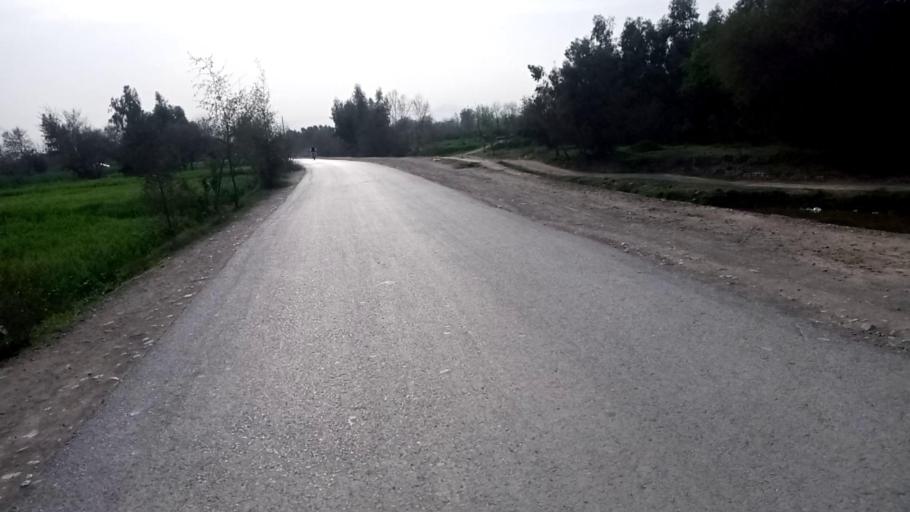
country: PK
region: Khyber Pakhtunkhwa
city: Peshawar
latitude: 34.0222
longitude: 71.4463
